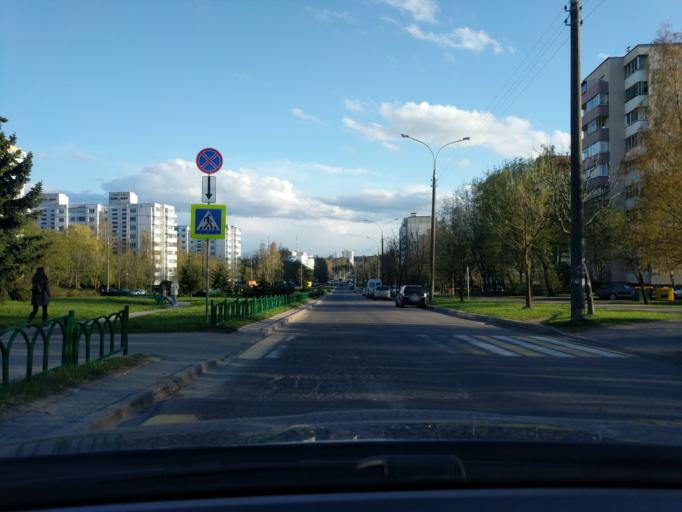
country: BY
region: Minsk
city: Novoye Medvezhino
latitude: 53.9031
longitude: 27.4527
